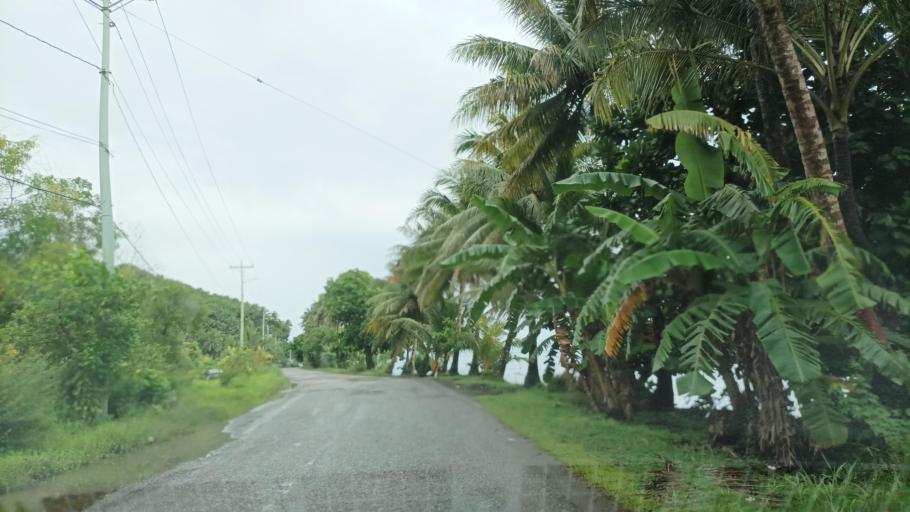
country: FM
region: Kosrae
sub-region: Tafunsak Municipality
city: Tafunsak
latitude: 5.3688
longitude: 163.0006
